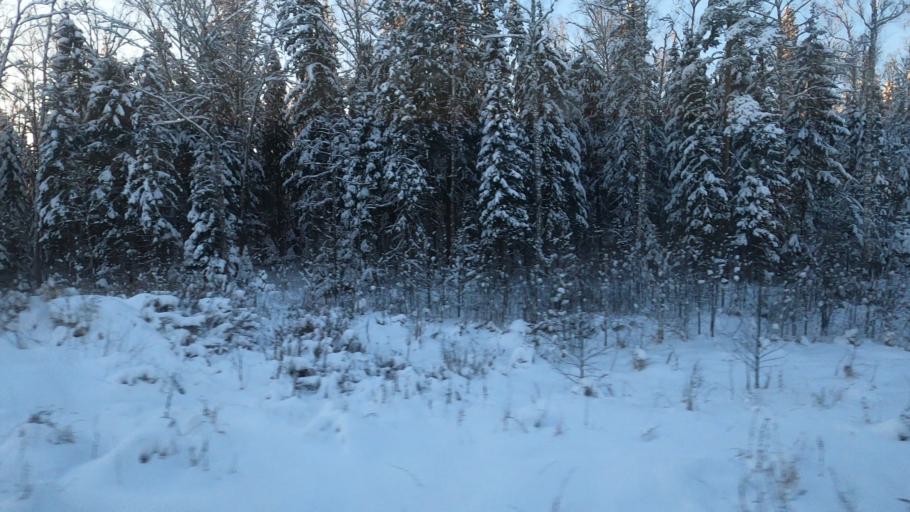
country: RU
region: Moskovskaya
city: Zhukovka
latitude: 56.4990
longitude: 37.5525
